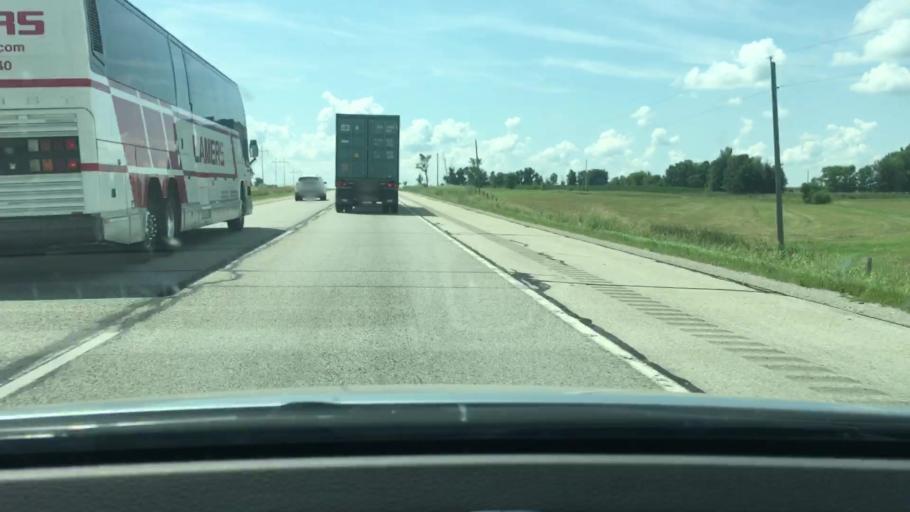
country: US
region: Wisconsin
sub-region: Fond du Lac County
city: Rosendale
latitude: 43.8966
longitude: -88.5839
